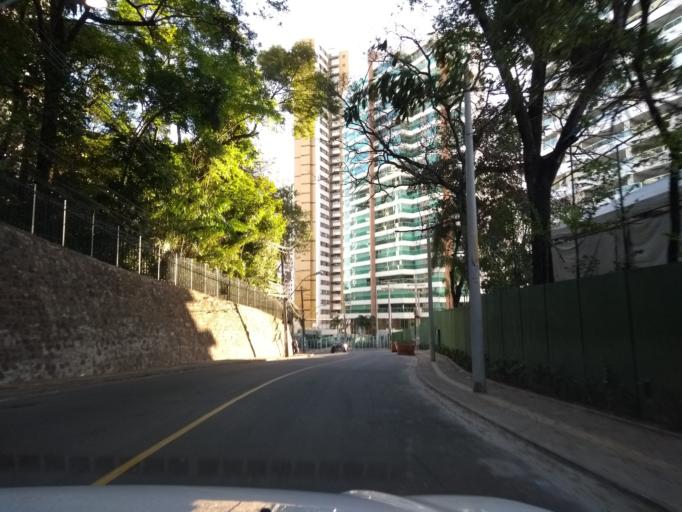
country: BR
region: Bahia
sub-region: Salvador
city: Salvador
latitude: -12.9973
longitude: -38.4865
